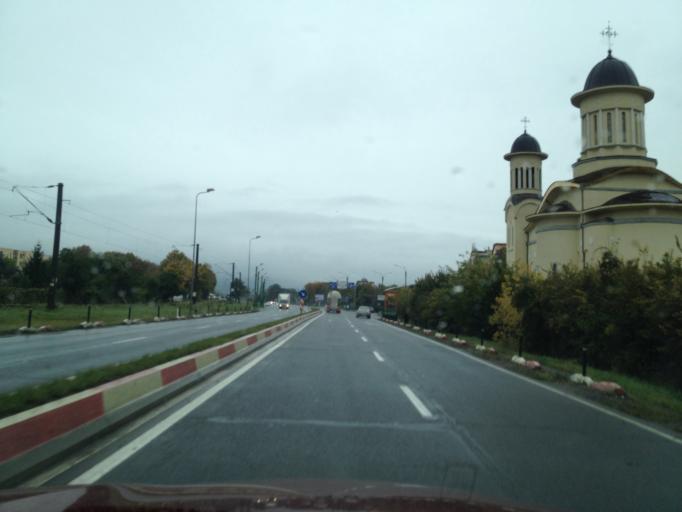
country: RO
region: Brasov
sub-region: Comuna Sanpetru
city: Sanpetru
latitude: 45.6768
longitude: 25.6499
